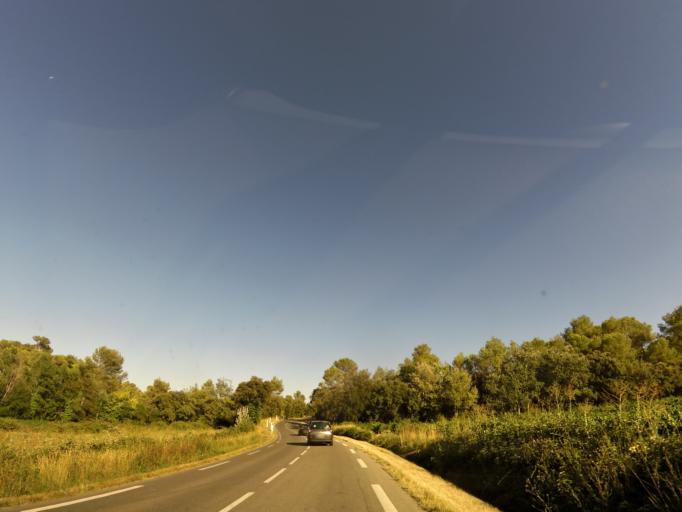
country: FR
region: Languedoc-Roussillon
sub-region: Departement du Gard
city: Sommieres
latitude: 43.8263
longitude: 4.0483
